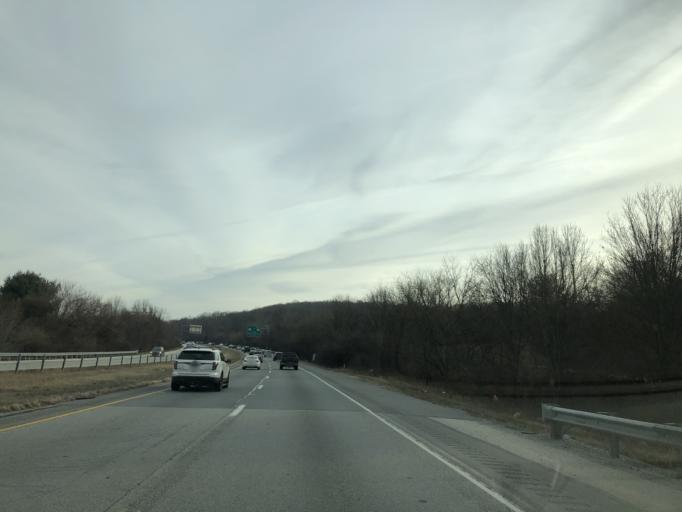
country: US
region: Pennsylvania
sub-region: Chester County
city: Exton
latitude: 40.0130
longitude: -75.6510
